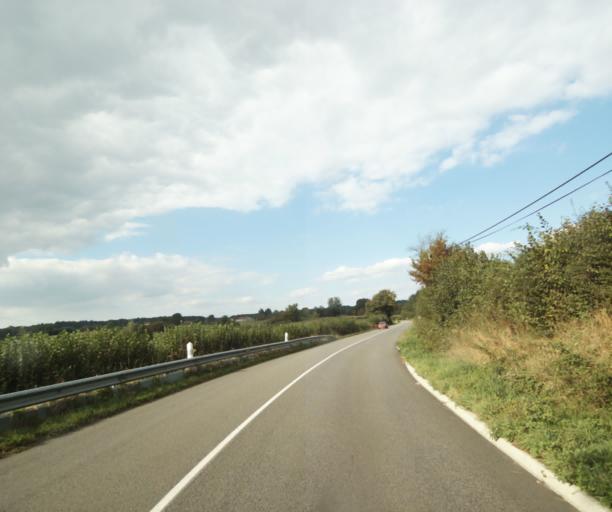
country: FR
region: Bourgogne
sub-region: Departement de Saone-et-Loire
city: Palinges
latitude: 46.5157
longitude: 4.2552
